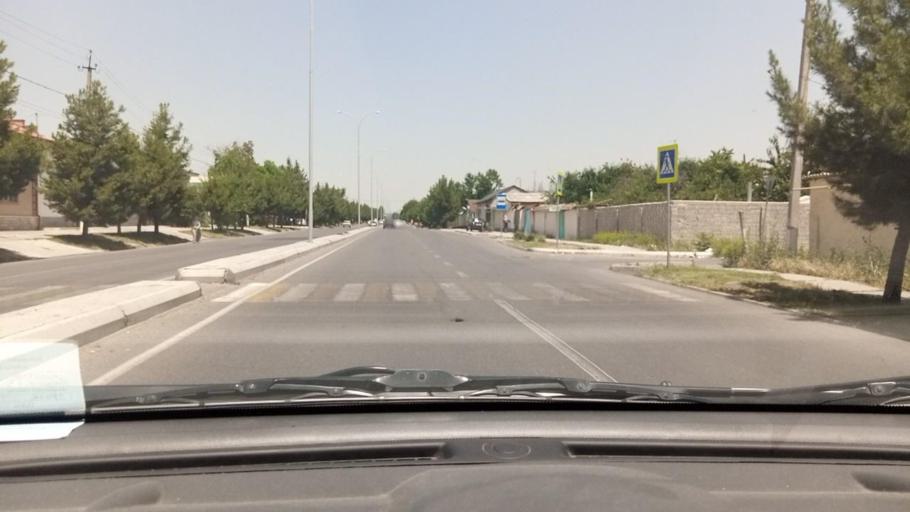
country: UZ
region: Toshkent Shahri
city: Tashkent
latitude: 41.2312
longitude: 69.1848
